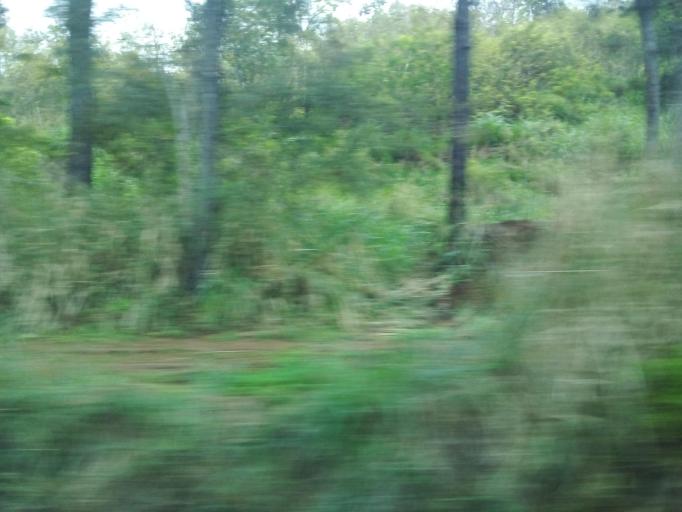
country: BR
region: Minas Gerais
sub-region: Rio Piracicaba
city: Rio Piracicaba
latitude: -19.8890
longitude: -43.1356
